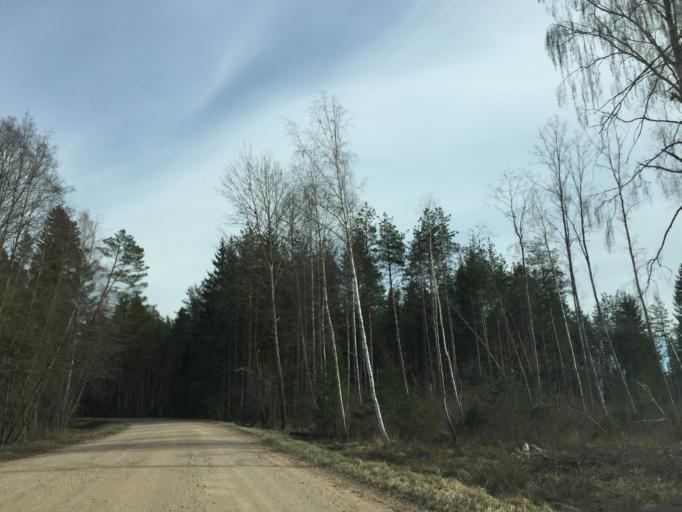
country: LV
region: Valkas Rajons
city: Valka
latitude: 57.8146
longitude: 25.8404
